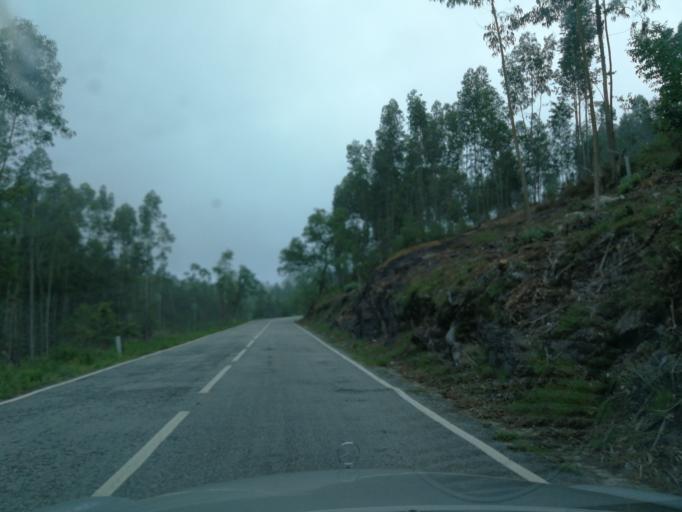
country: PT
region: Braga
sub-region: Braga
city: Braga
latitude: 41.5190
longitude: -8.3797
